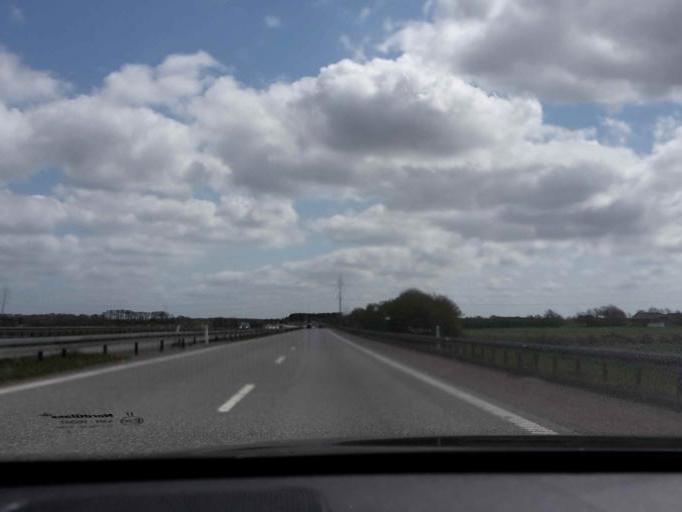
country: DK
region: South Denmark
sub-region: Esbjerg Kommune
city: Tjaereborg
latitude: 55.5143
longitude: 8.6297
